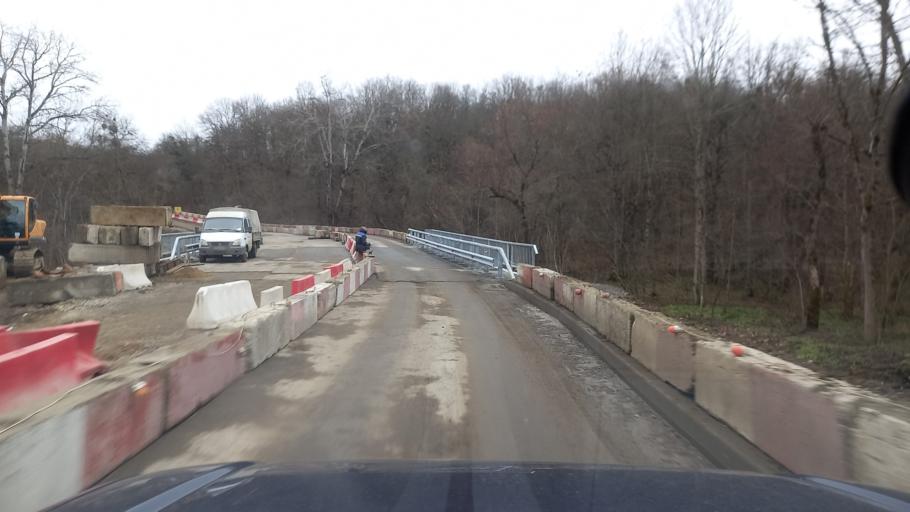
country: RU
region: Krasnodarskiy
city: Goryachiy Klyuch
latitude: 44.5551
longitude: 39.2492
